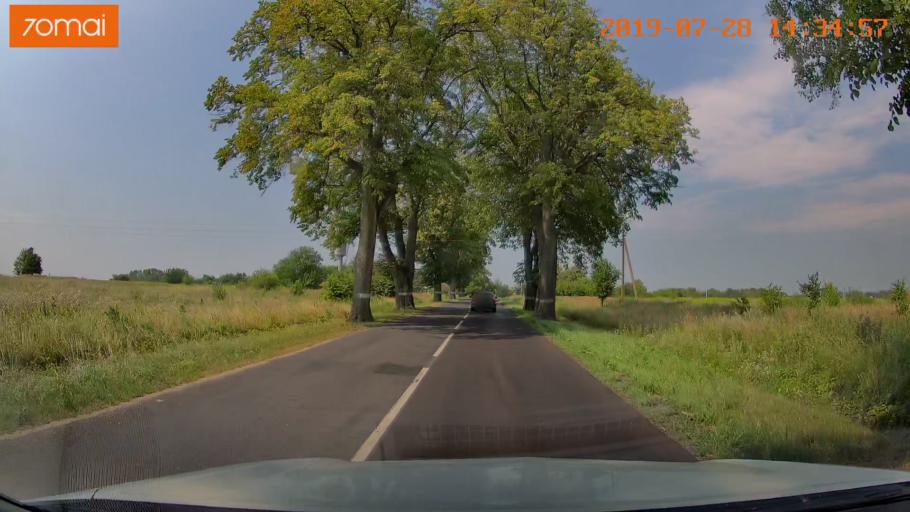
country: RU
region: Kaliningrad
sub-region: Gorod Kaliningrad
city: Yantarnyy
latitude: 54.8282
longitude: 20.0127
